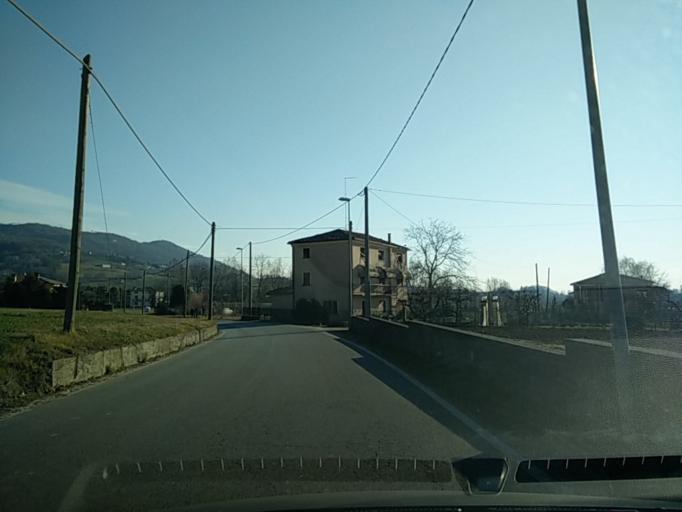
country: IT
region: Veneto
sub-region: Provincia di Treviso
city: Sarmede
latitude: 45.9760
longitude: 12.3891
